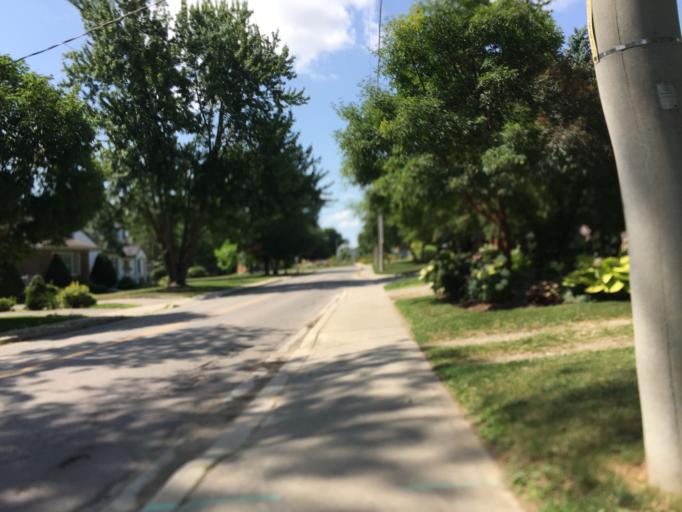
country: CA
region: Ontario
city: Stratford
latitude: 43.3781
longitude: -80.9868
